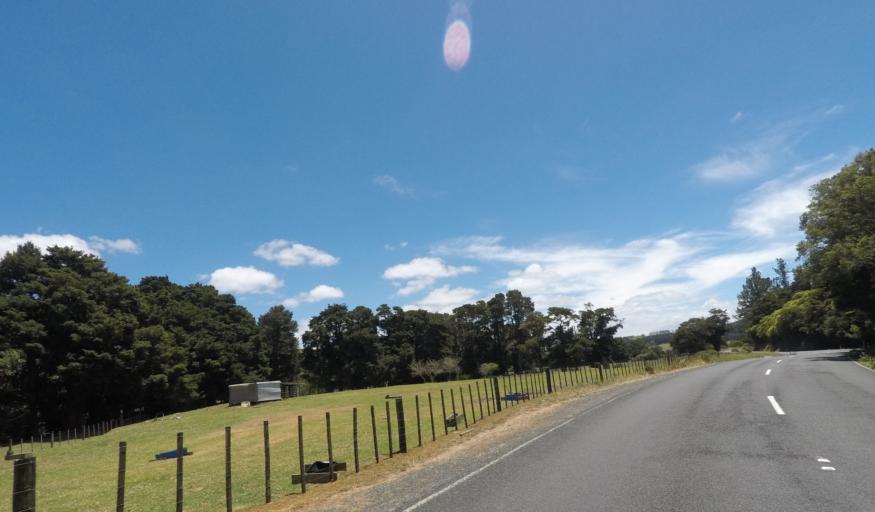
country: NZ
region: Northland
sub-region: Whangarei
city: Whangarei
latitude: -35.5401
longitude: 174.3102
